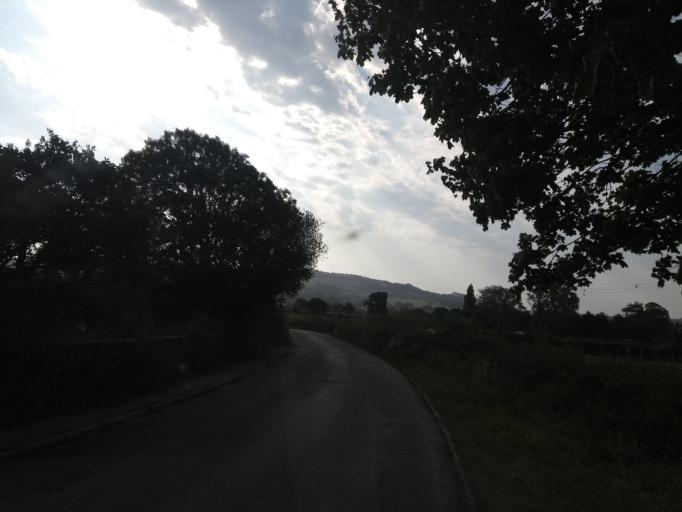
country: GB
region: England
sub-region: Devon
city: Colyton
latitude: 50.7528
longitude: -3.0467
